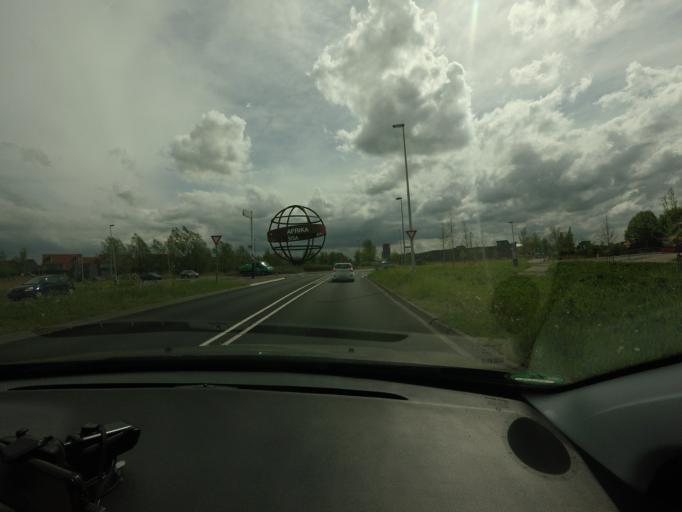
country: NL
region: North Holland
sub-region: Gemeente Purmerend
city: Purmerend
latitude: 52.5010
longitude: 4.9383
